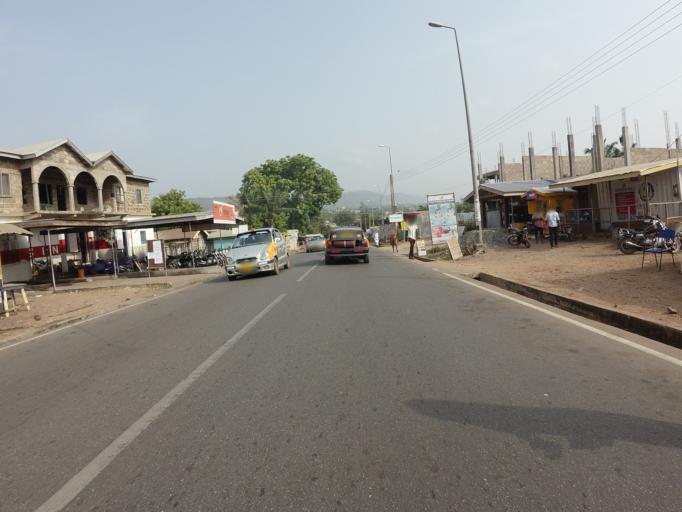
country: GH
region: Volta
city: Ho
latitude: 6.6101
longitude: 0.4748
